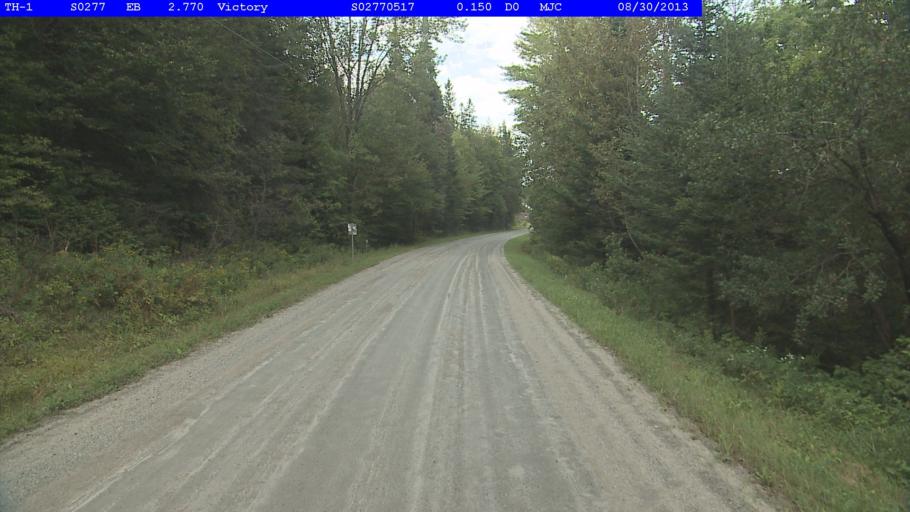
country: US
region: Vermont
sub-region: Caledonia County
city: Lyndonville
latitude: 44.4984
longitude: -71.8541
